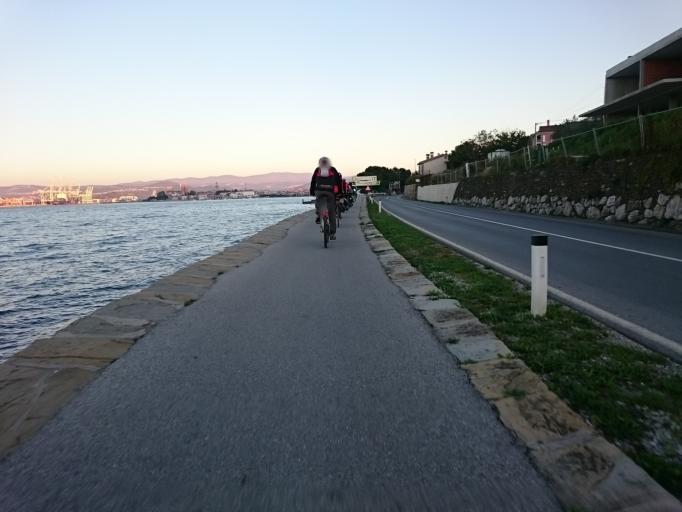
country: SI
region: Koper-Capodistria
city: Koper
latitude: 45.5471
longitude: 13.7066
